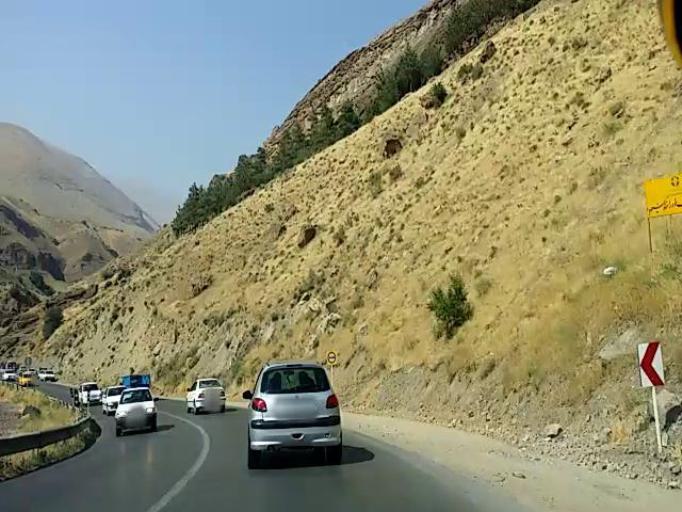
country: IR
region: Alborz
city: Karaj
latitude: 35.9181
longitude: 51.0500
